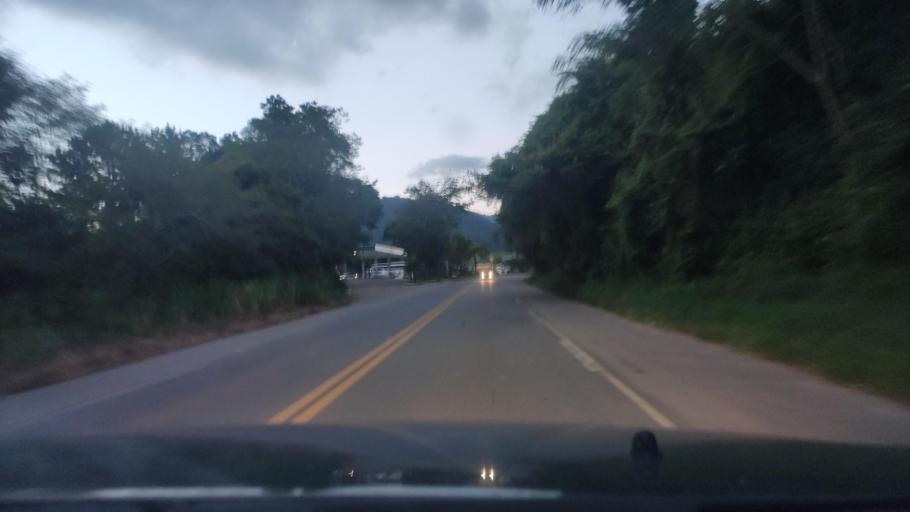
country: BR
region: Sao Paulo
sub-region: Campos Do Jordao
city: Campos do Jordao
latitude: -22.7565
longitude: -45.7428
